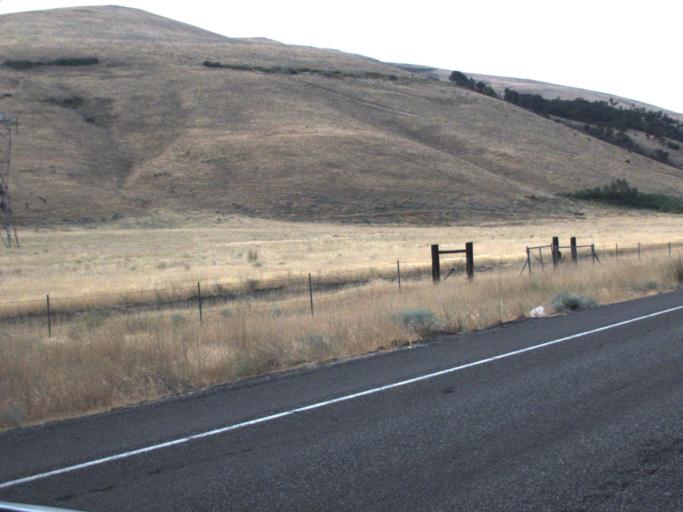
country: US
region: Washington
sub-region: Klickitat County
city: Goldendale
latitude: 46.0853
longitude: -120.5526
